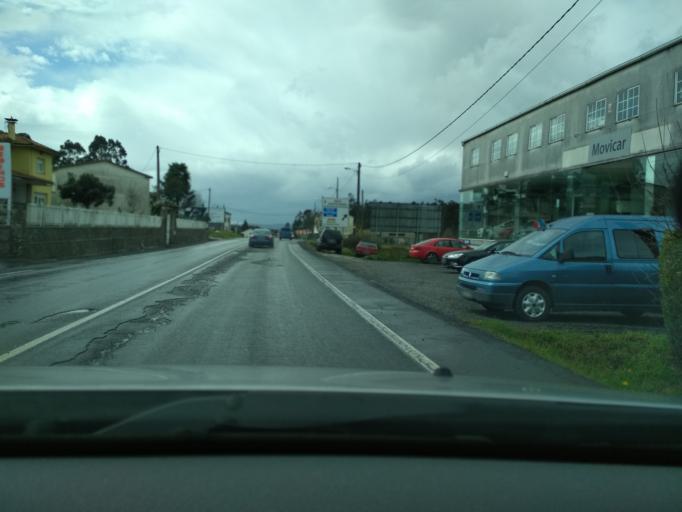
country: ES
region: Galicia
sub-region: Provincia da Coruna
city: Santiago de Compostela
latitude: 42.8365
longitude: -8.5864
